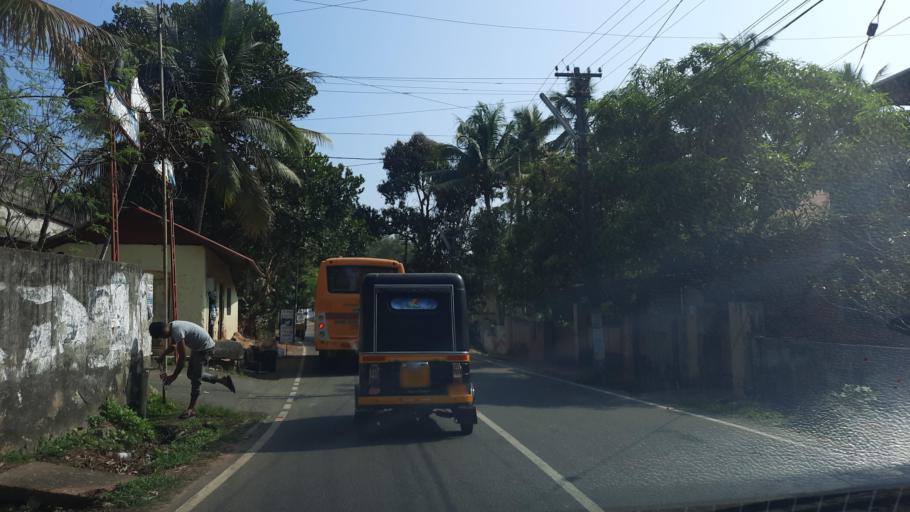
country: IN
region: Kerala
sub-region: Thiruvananthapuram
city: Nedumangad
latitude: 8.5689
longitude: 76.9231
